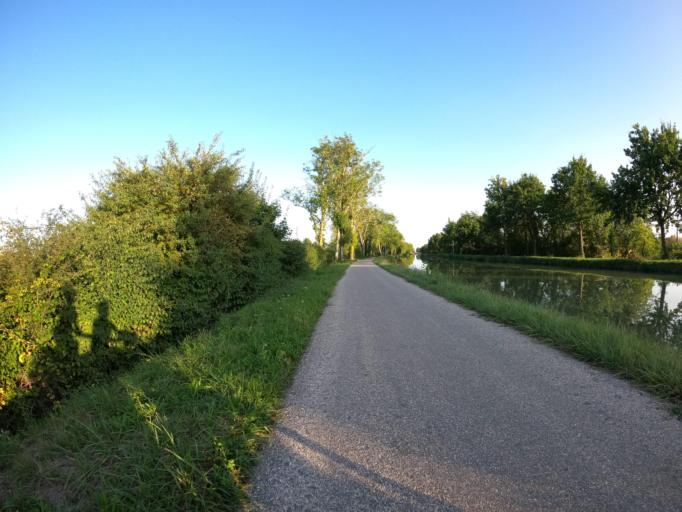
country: FR
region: Midi-Pyrenees
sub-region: Departement du Tarn-et-Garonne
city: Saint-Porquier
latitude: 44.0230
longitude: 1.1636
